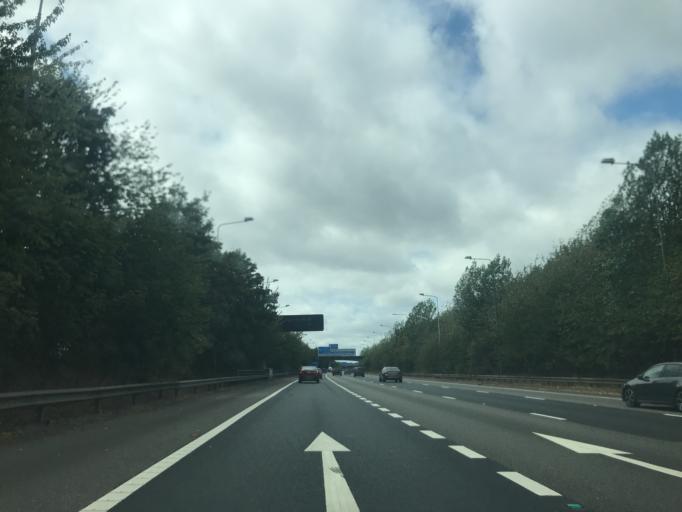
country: GB
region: England
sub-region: Greater London
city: West Drayton
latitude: 51.4945
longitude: -0.4706
